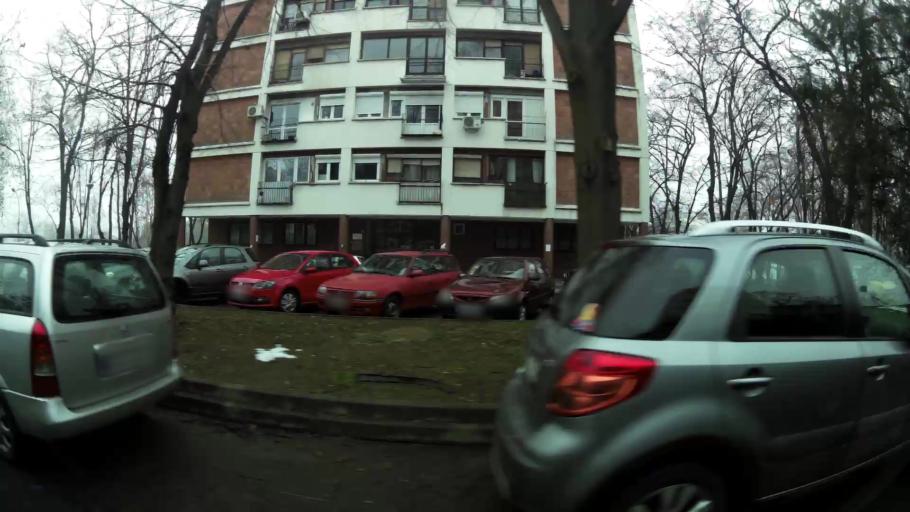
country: RS
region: Central Serbia
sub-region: Belgrade
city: Savski Venac
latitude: 44.7874
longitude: 20.4625
